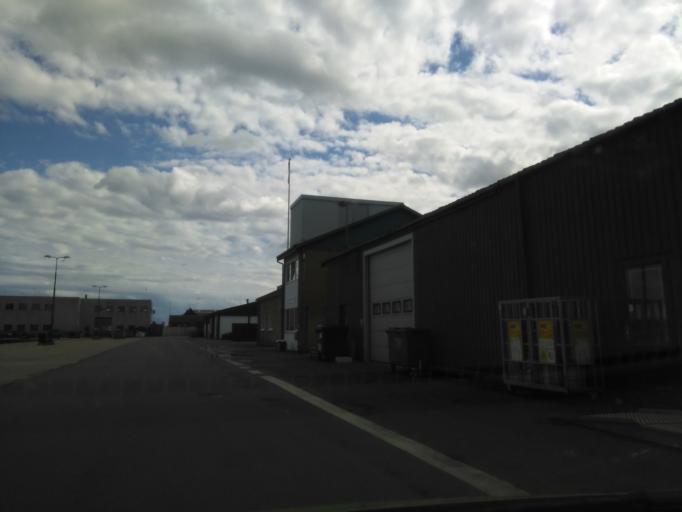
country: DK
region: Capital Region
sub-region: Bornholm Kommune
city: Nexo
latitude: 55.0610
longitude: 15.1349
